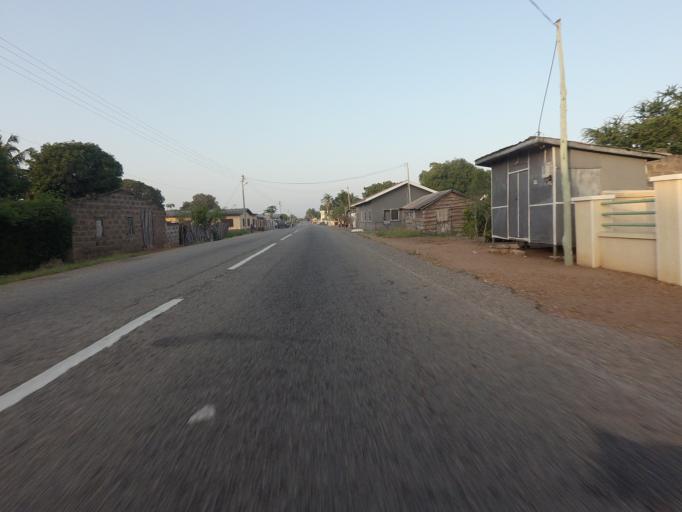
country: GH
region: Volta
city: Anloga
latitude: 5.7824
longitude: 0.8440
